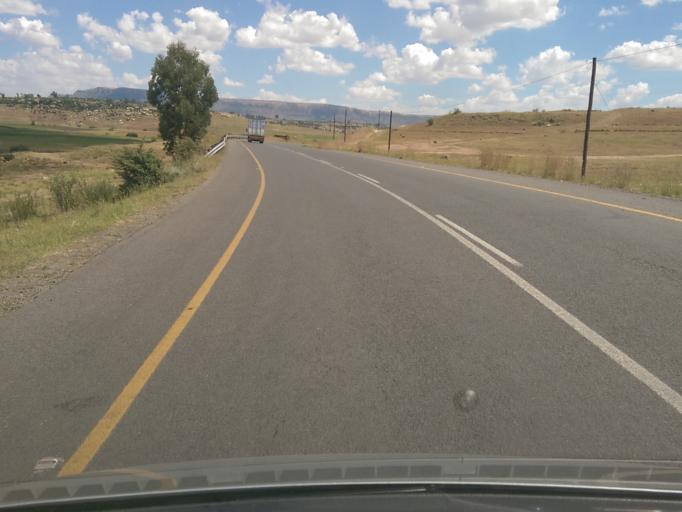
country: LS
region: Maseru
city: Maseru
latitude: -29.3908
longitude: 27.5483
